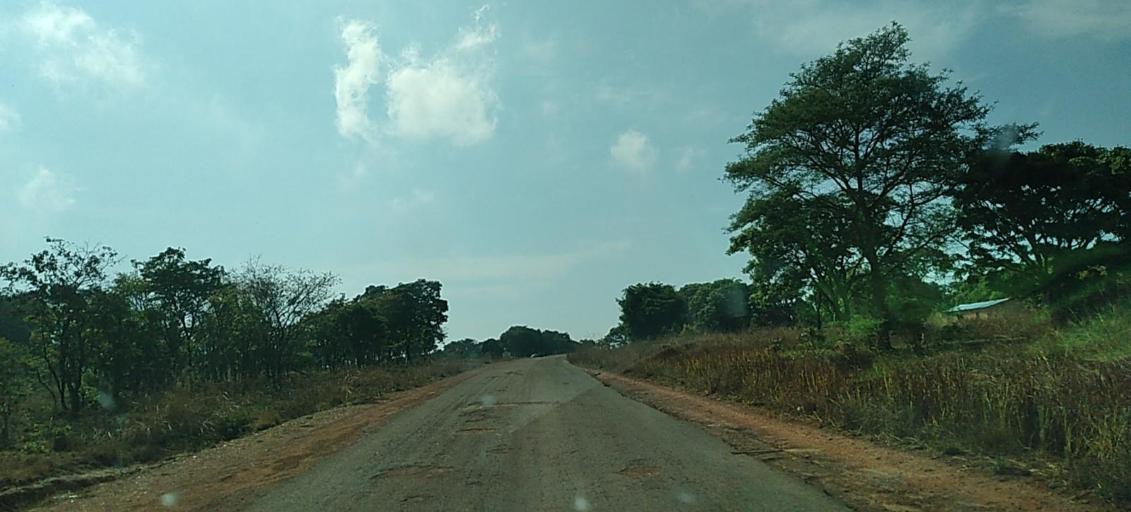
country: ZM
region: North-Western
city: Mwinilunga
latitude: -11.7714
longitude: 25.0113
